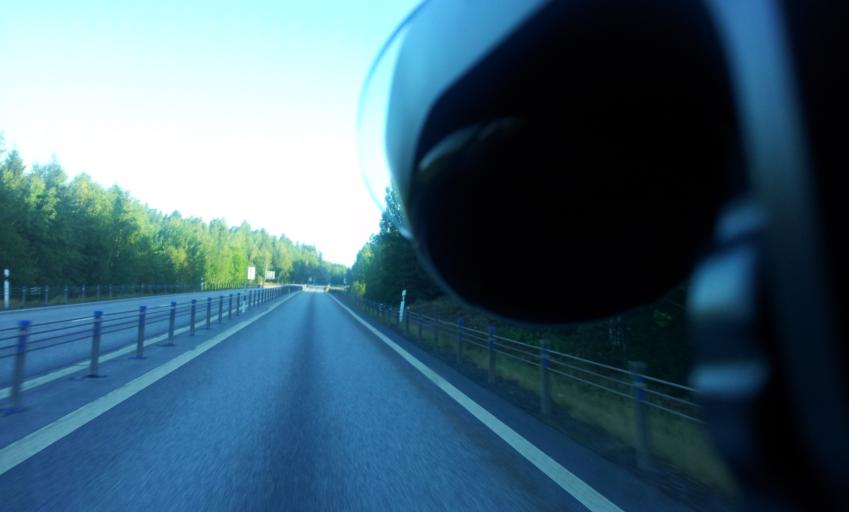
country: SE
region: OEstergoetland
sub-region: Valdemarsviks Kommun
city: Valdemarsvik
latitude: 58.1658
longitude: 16.5408
